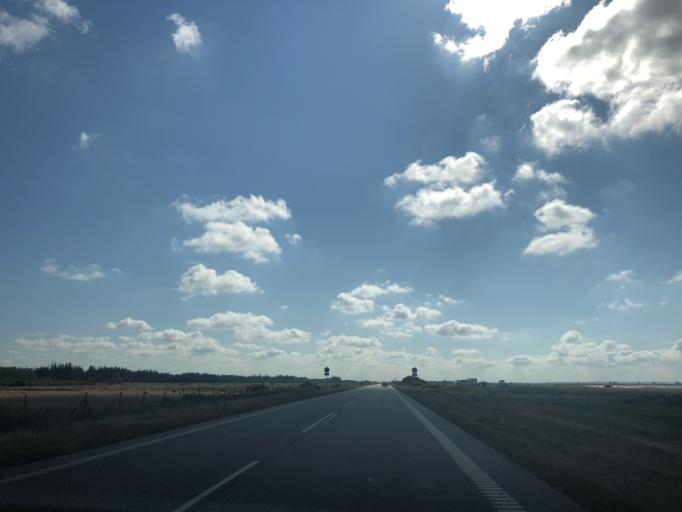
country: DK
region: North Denmark
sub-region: Vesthimmerland Kommune
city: Logstor
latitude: 57.0245
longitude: 9.0177
